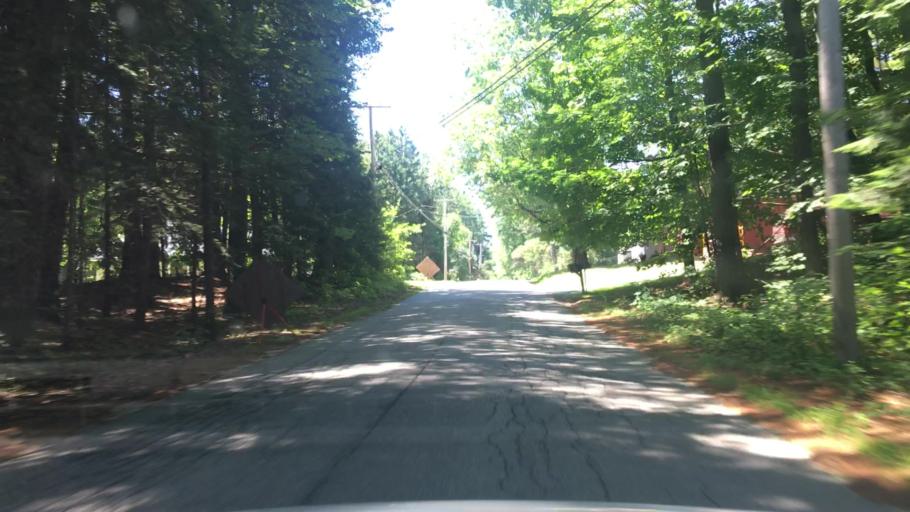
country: US
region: New Hampshire
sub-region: Merrimack County
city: Hopkinton
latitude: 43.1992
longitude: -71.6707
